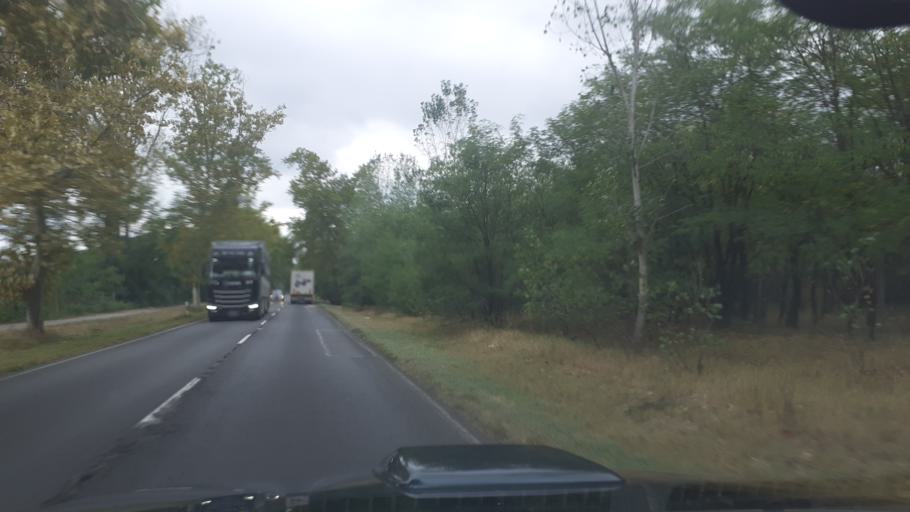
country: HU
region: Bacs-Kiskun
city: Balloszog
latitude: 46.8885
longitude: 19.5875
